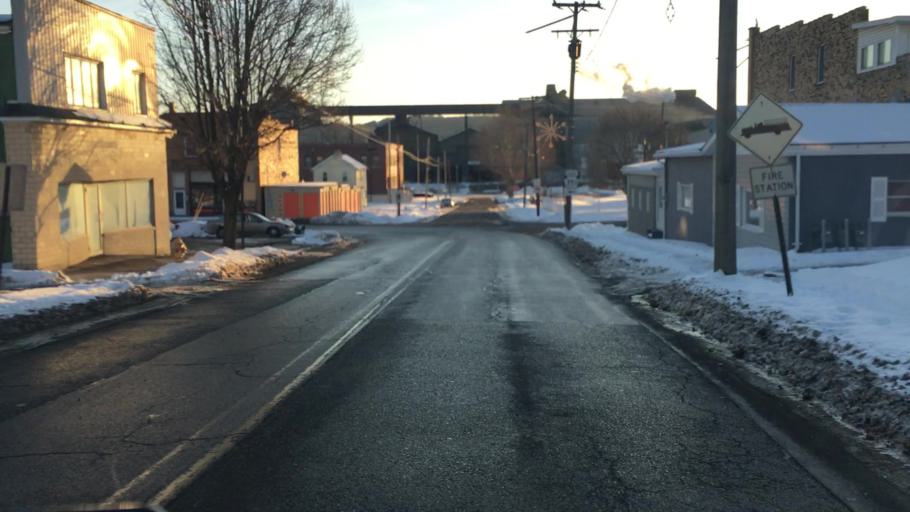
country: US
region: Pennsylvania
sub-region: Beaver County
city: Big Beaver
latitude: 40.8342
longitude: -80.3238
